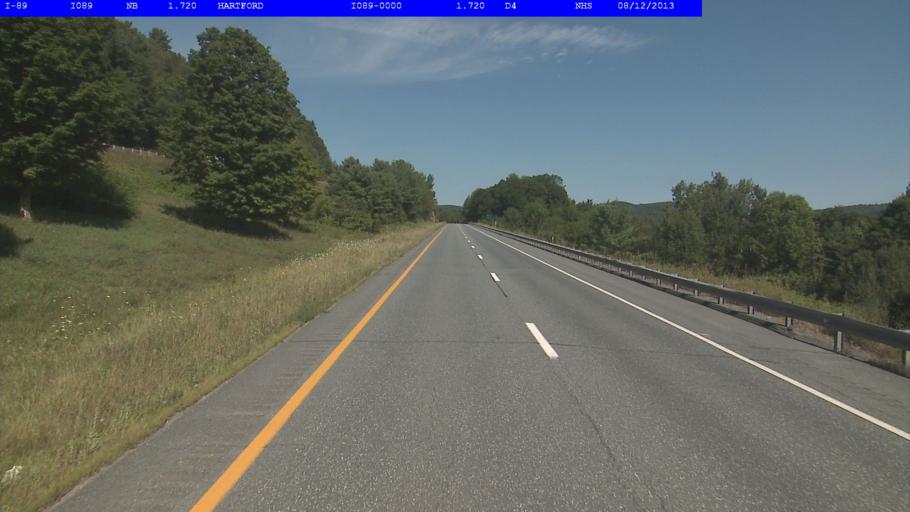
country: US
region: Vermont
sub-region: Windsor County
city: White River Junction
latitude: 43.6539
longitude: -72.3479
